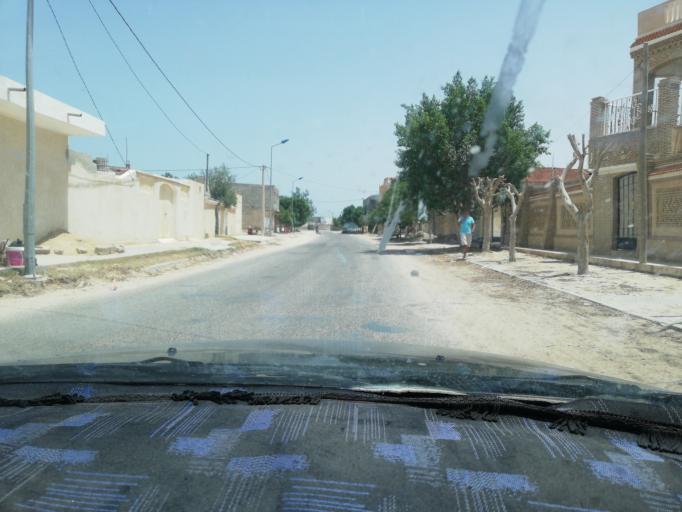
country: TN
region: Qabis
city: Matmata
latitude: 33.6197
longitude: 10.2746
